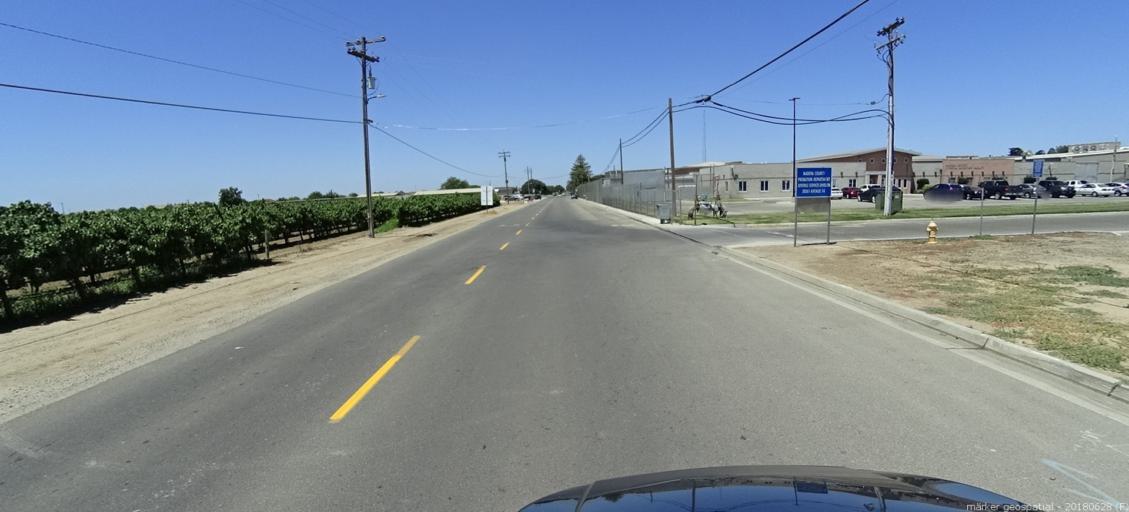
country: US
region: California
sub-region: Madera County
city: Parksdale
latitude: 36.9526
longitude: -120.0341
